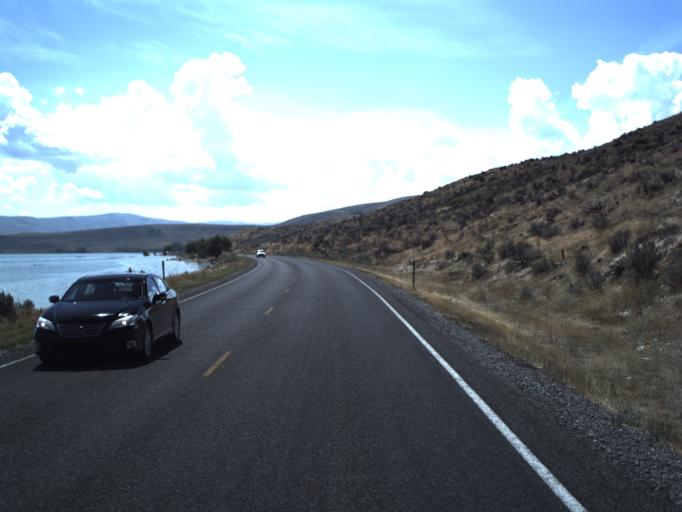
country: US
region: Utah
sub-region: Rich County
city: Randolph
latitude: 41.8725
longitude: -111.3654
